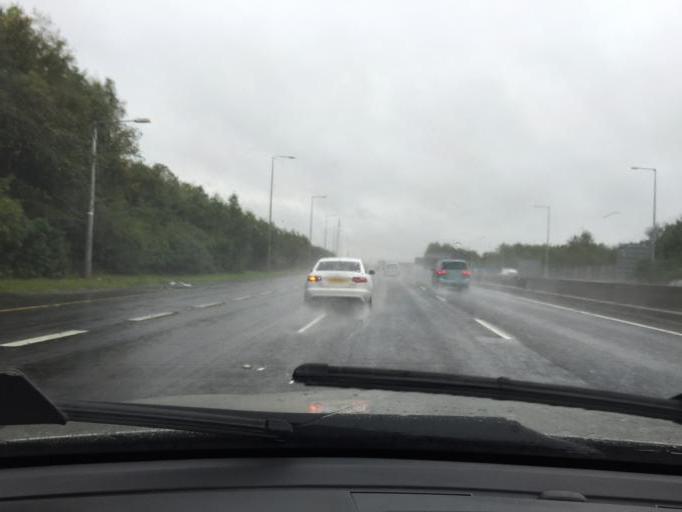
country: IE
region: Leinster
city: Castleknock
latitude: 53.3748
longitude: -6.3716
